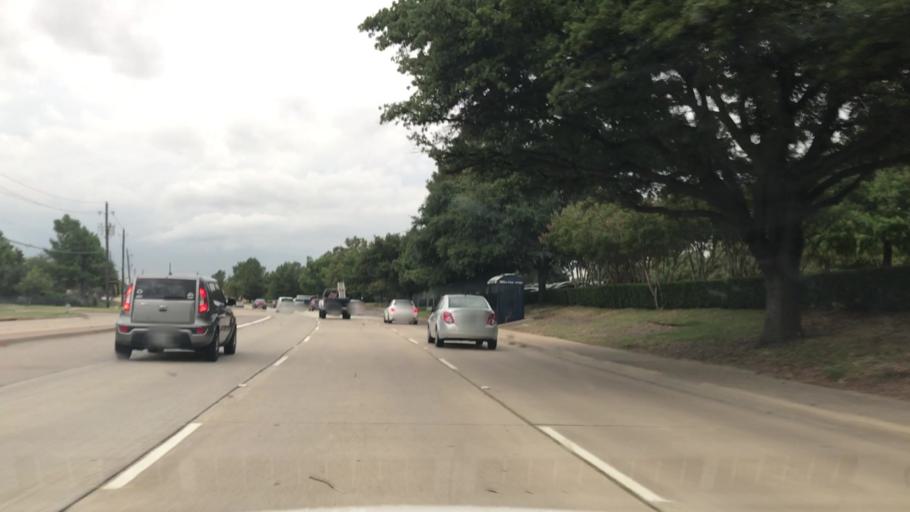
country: US
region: Texas
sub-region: Denton County
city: The Colony
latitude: 33.0289
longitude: -96.8840
